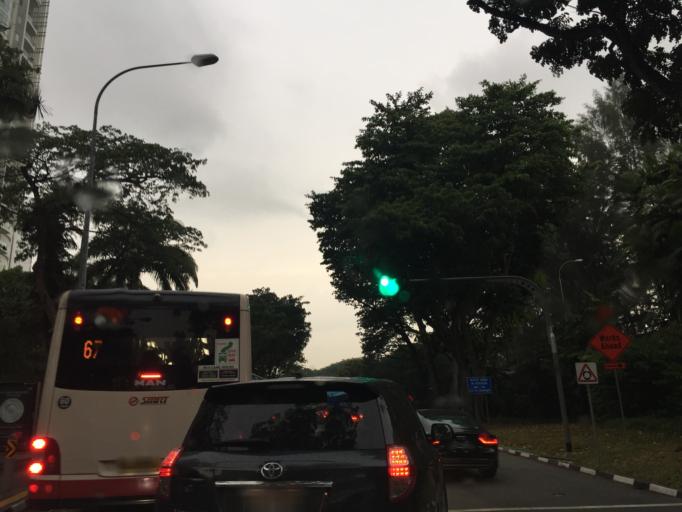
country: SG
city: Singapore
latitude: 1.3142
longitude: 103.8385
